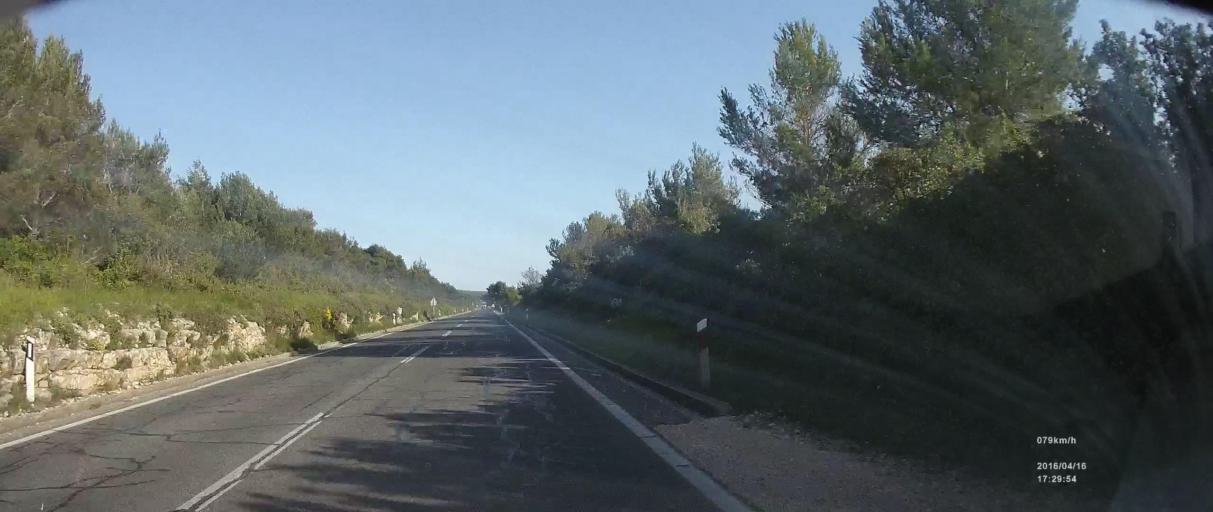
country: HR
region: Zadarska
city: Sukosan
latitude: 44.0270
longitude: 15.3477
